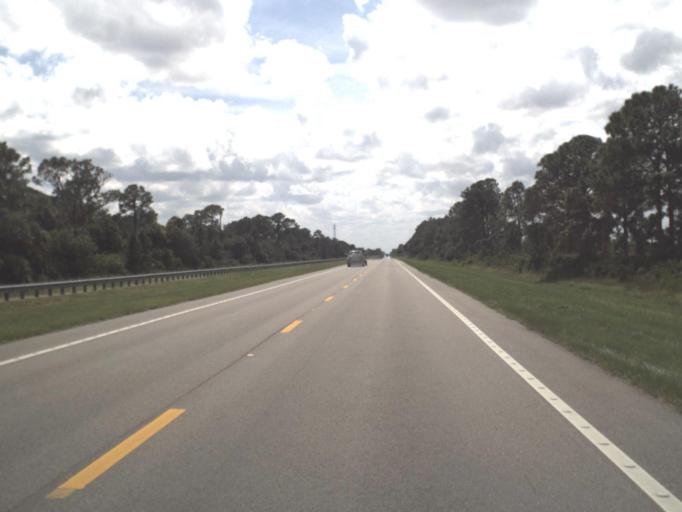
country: US
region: Florida
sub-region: Collier County
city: Immokalee
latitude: 26.3354
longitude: -81.3434
